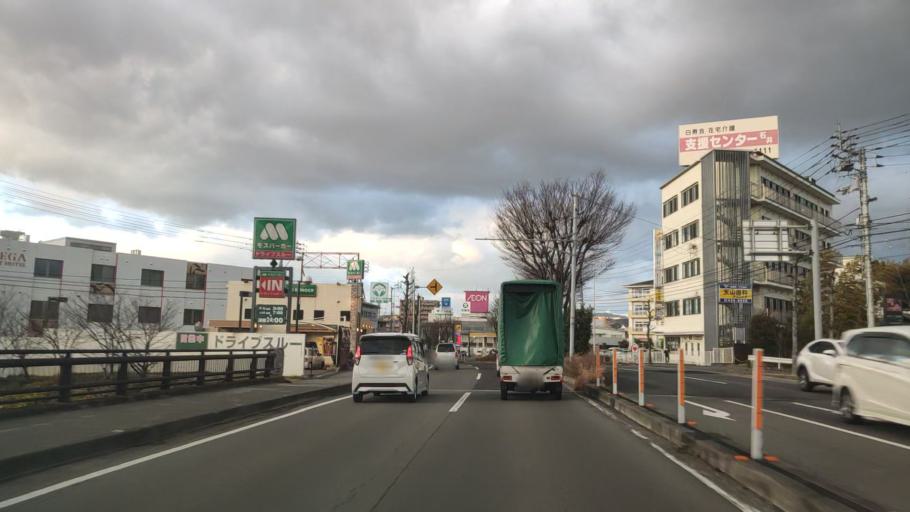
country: JP
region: Ehime
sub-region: Shikoku-chuo Shi
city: Matsuyama
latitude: 33.8178
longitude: 132.7771
